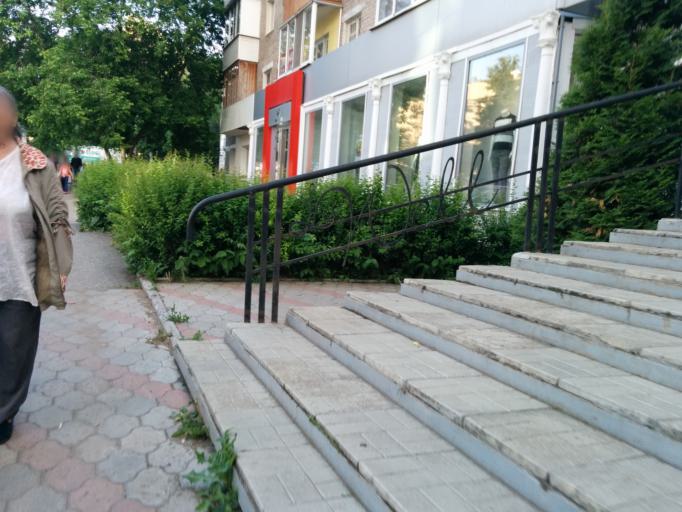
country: RU
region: Perm
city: Perm
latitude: 58.0069
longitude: 56.2483
